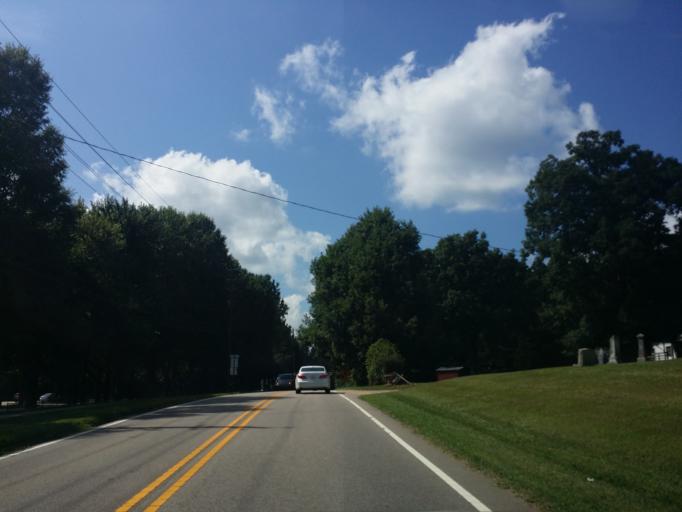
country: US
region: North Carolina
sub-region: Wake County
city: West Raleigh
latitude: 35.8912
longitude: -78.7144
